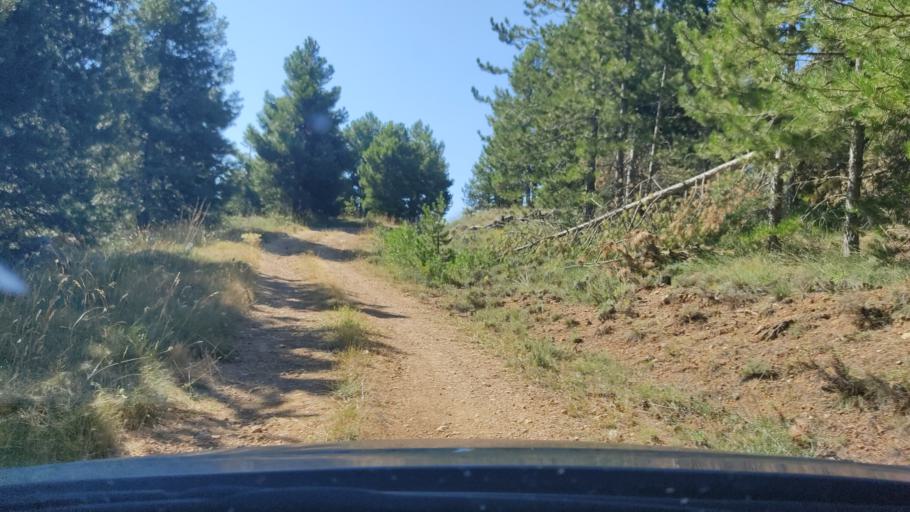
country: ES
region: Aragon
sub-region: Provincia de Teruel
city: Monforte de Moyuela
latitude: 41.0355
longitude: -1.0426
